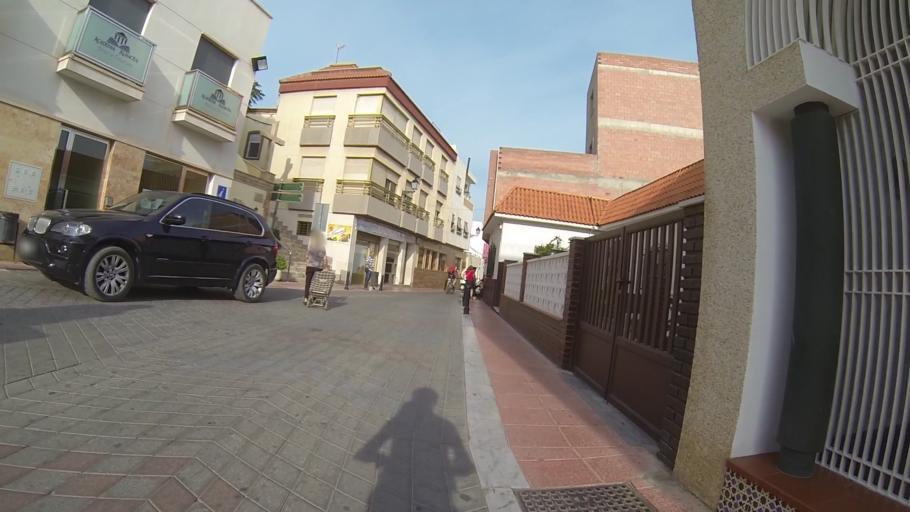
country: ES
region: Andalusia
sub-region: Provincia de Almeria
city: Alhama de Almeria
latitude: 36.9583
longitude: -2.5711
